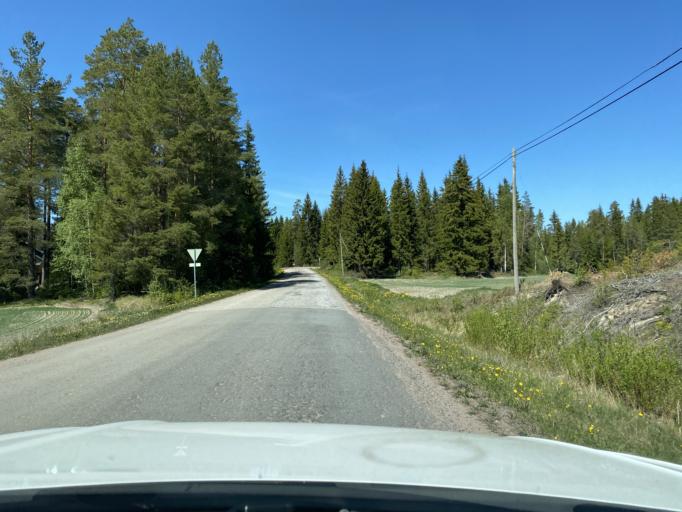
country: FI
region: Satakunta
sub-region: Rauma
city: Kiukainen
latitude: 61.1324
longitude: 21.9884
